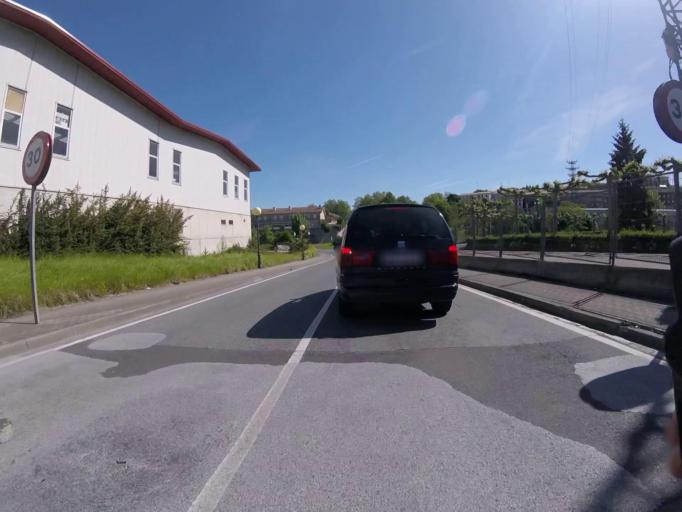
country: ES
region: Basque Country
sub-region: Provincia de Guipuzcoa
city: Irun
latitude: 43.3263
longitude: -1.8219
